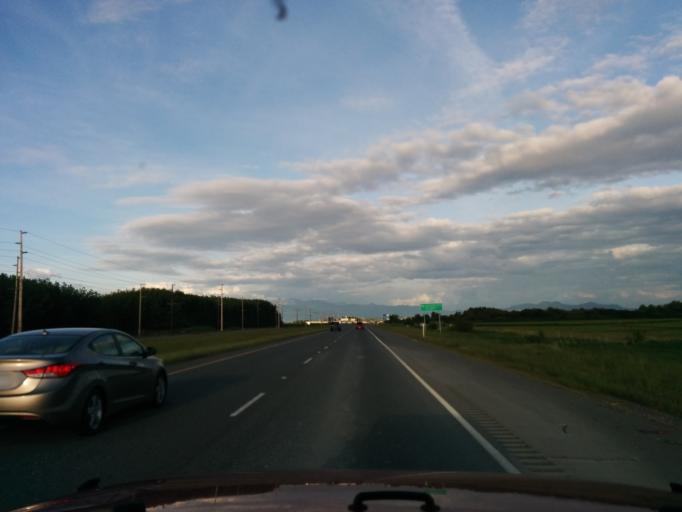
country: US
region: Washington
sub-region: Skagit County
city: Anacortes
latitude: 48.4515
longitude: -122.4938
